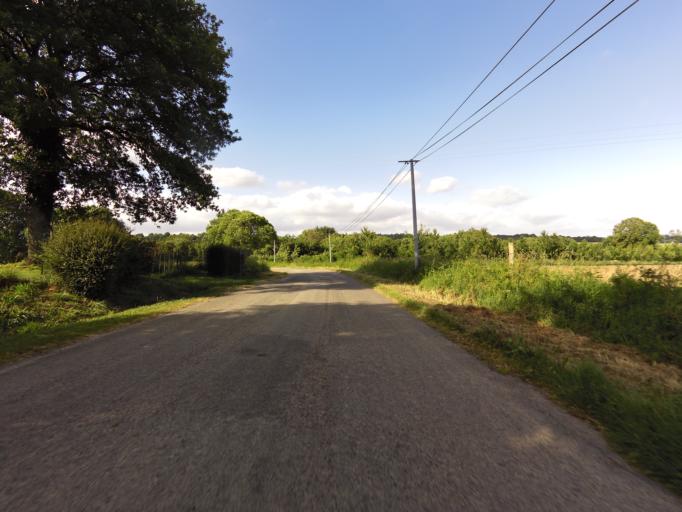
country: FR
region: Brittany
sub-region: Departement du Morbihan
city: Molac
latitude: 47.7148
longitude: -2.4142
